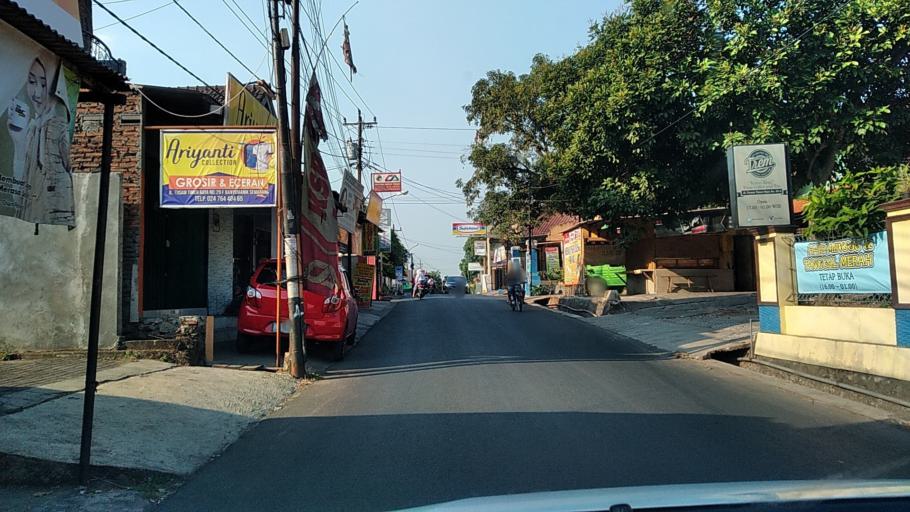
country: ID
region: Central Java
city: Ungaran
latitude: -7.0680
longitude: 110.4268
